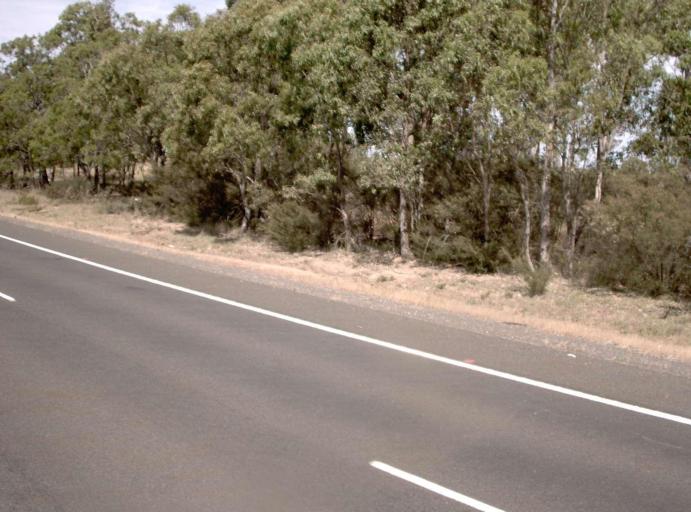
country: AU
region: Victoria
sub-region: East Gippsland
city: Bairnsdale
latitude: -37.8886
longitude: 147.3918
